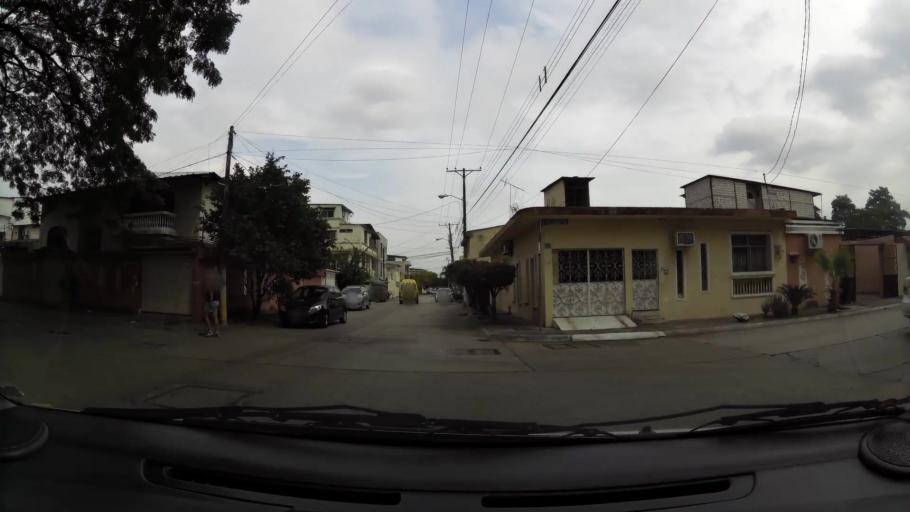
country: EC
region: Guayas
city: Eloy Alfaro
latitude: -2.1162
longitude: -79.8941
